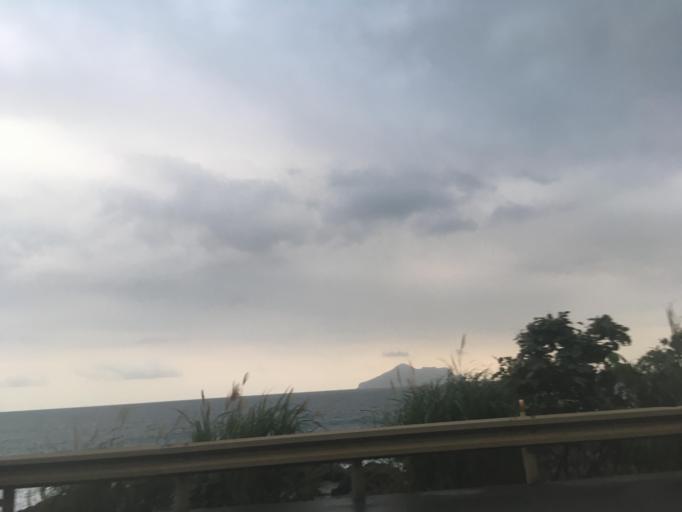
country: TW
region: Taiwan
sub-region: Yilan
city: Yilan
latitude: 24.9093
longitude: 121.8746
